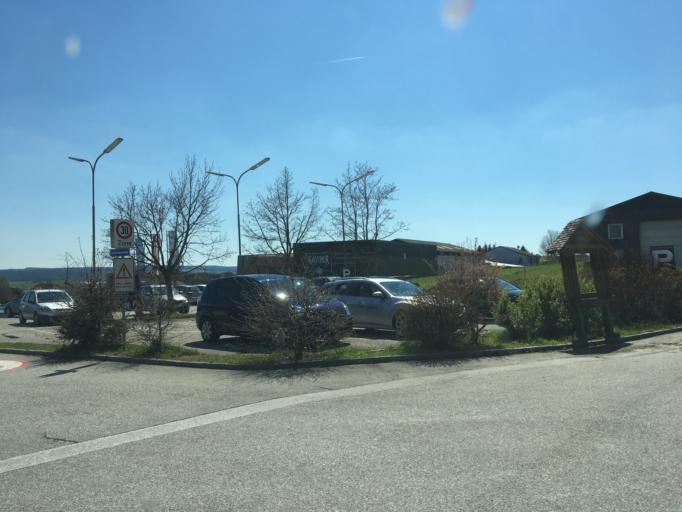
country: AT
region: Upper Austria
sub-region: Politischer Bezirk Urfahr-Umgebung
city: Bad Leonfelden
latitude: 48.5261
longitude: 14.3005
